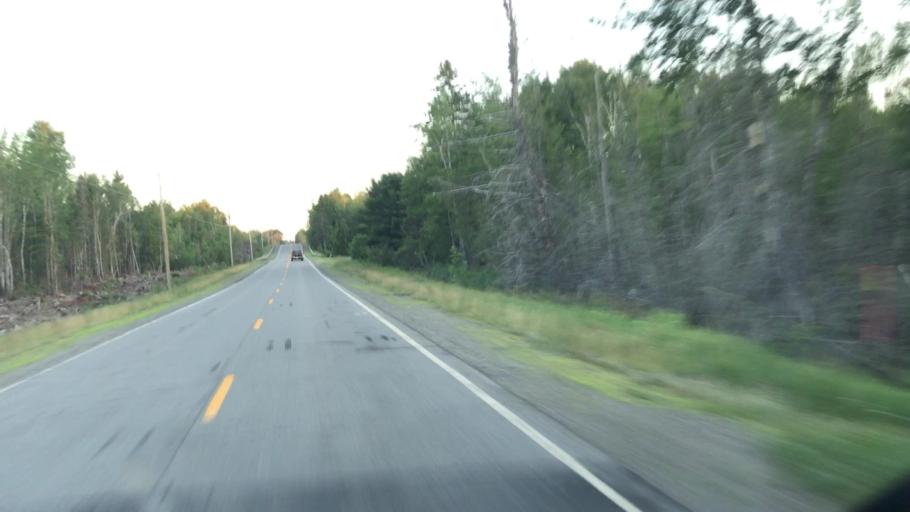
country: US
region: Maine
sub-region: Penobscot County
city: Medway
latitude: 45.6044
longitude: -68.3080
